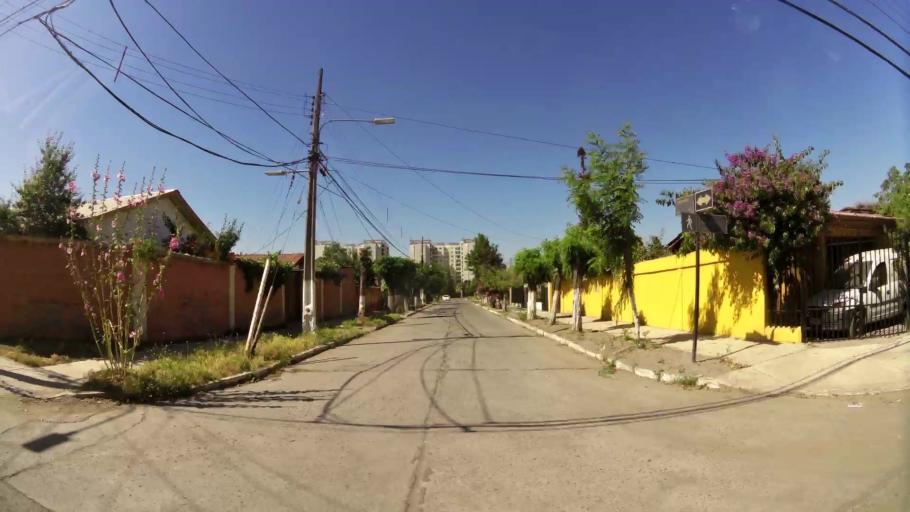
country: CL
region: Santiago Metropolitan
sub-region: Provincia de Santiago
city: La Pintana
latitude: -33.5428
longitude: -70.6564
